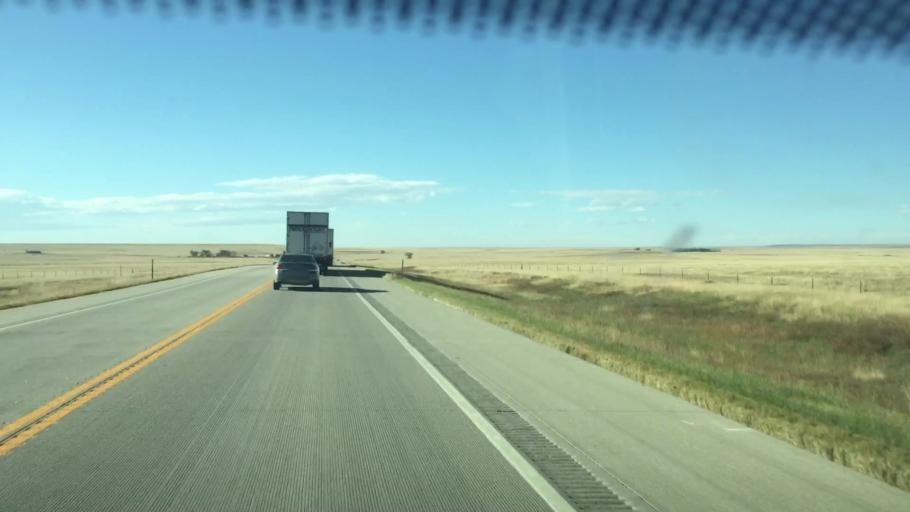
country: US
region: Colorado
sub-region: Lincoln County
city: Hugo
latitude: 38.9245
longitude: -103.1900
